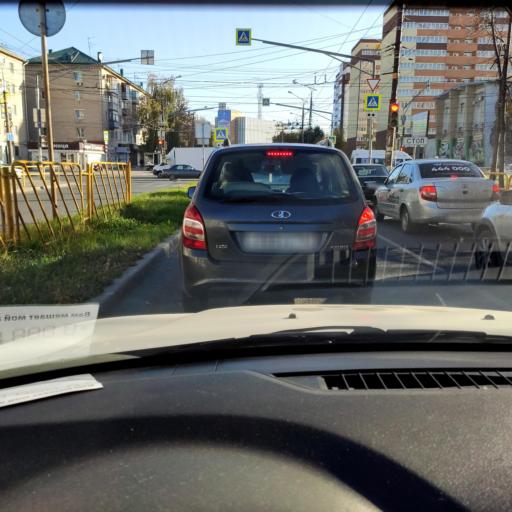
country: RU
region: Samara
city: Tol'yatti
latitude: 53.5221
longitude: 49.4141
